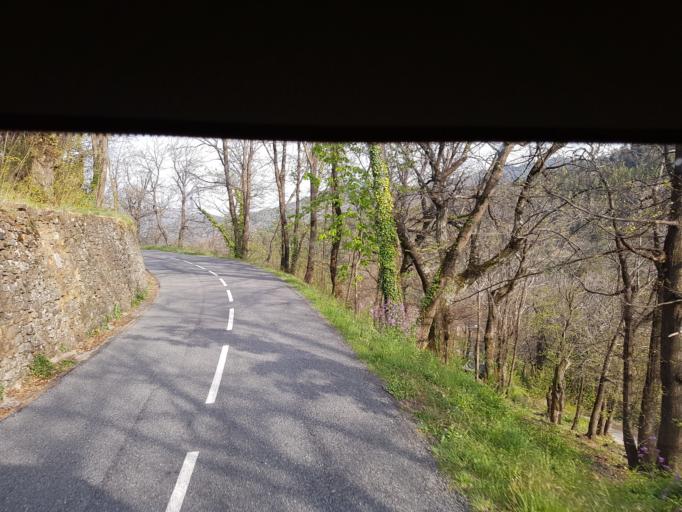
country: FR
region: Languedoc-Roussillon
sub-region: Departement du Gard
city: Branoux-les-Taillades
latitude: 44.3300
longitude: 3.8939
